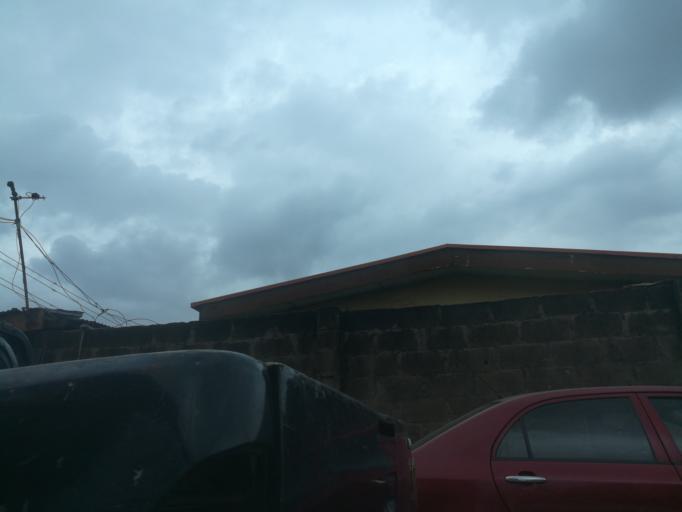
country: NG
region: Lagos
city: Ikeja
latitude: 6.6017
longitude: 3.3456
